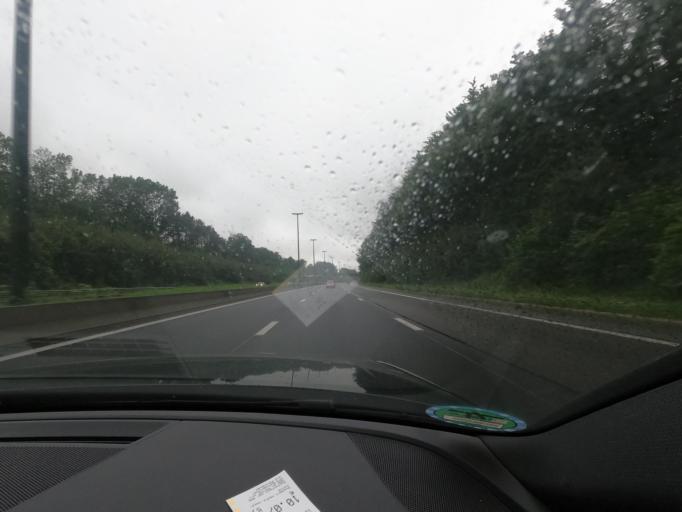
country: BE
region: Wallonia
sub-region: Province du Hainaut
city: Chapelle-lez-Herlaimont
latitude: 50.4792
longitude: 4.2888
